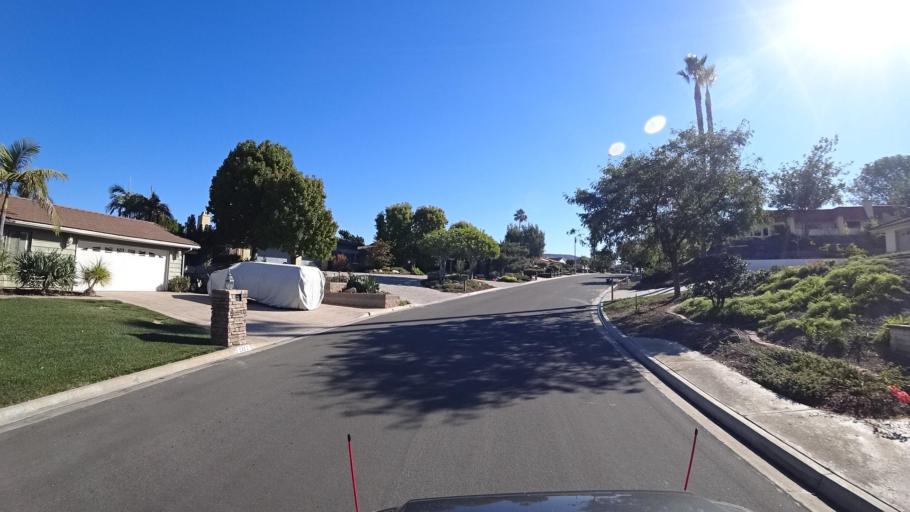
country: US
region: California
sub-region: San Diego County
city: Bonita
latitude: 32.6744
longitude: -117.0069
